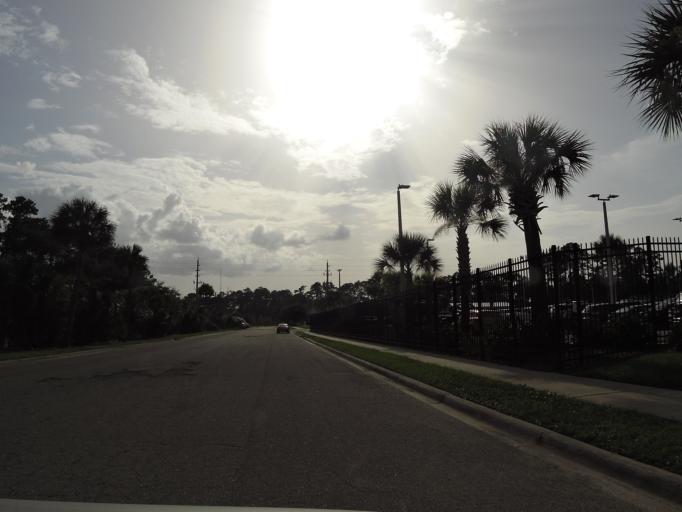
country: US
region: Florida
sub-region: Duval County
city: Jacksonville
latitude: 30.2890
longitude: -81.7335
